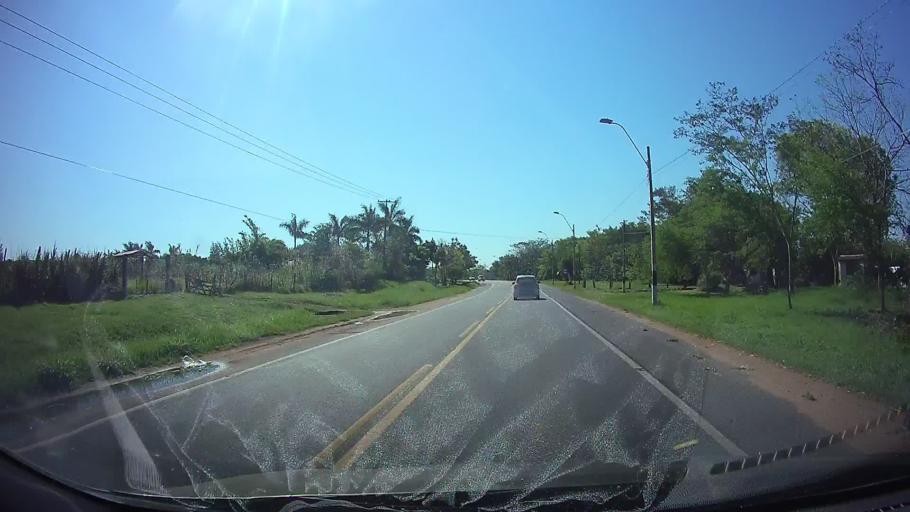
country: PY
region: Central
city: Aregua
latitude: -25.3270
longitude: -57.3616
